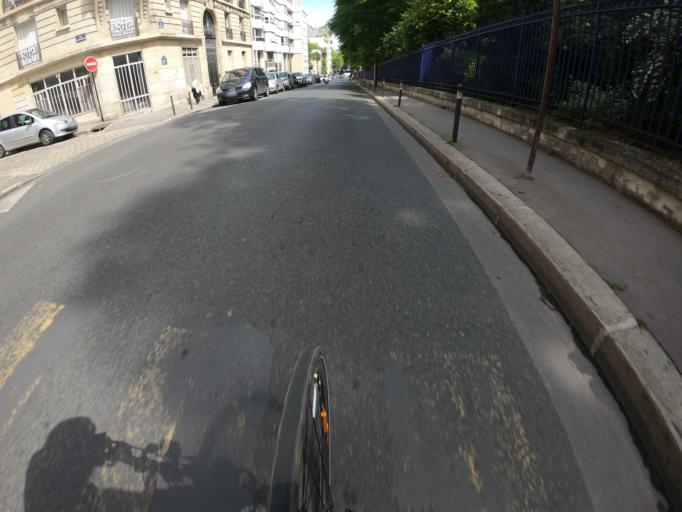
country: FR
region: Ile-de-France
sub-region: Departement du Val-de-Marne
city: Gentilly
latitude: 48.8224
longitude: 2.3352
